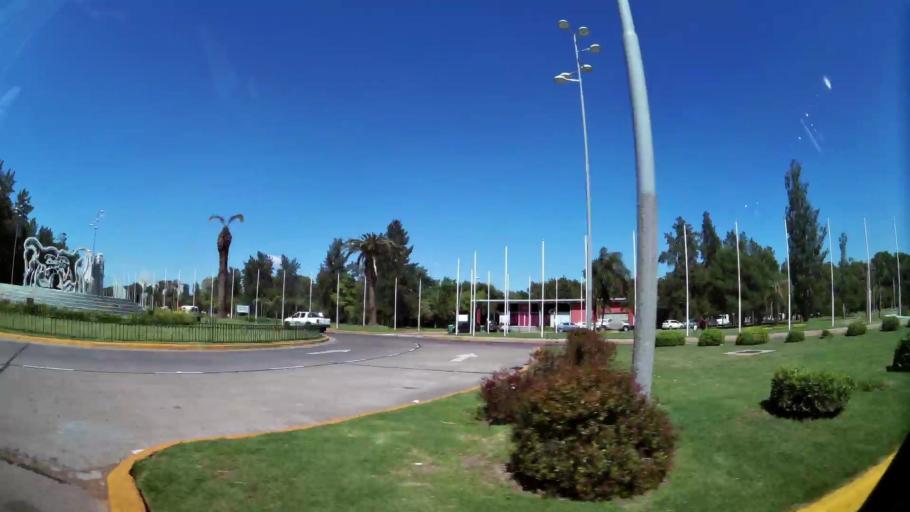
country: AR
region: Buenos Aires
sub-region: Partido de Tigre
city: Tigre
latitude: -34.4251
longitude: -58.5826
